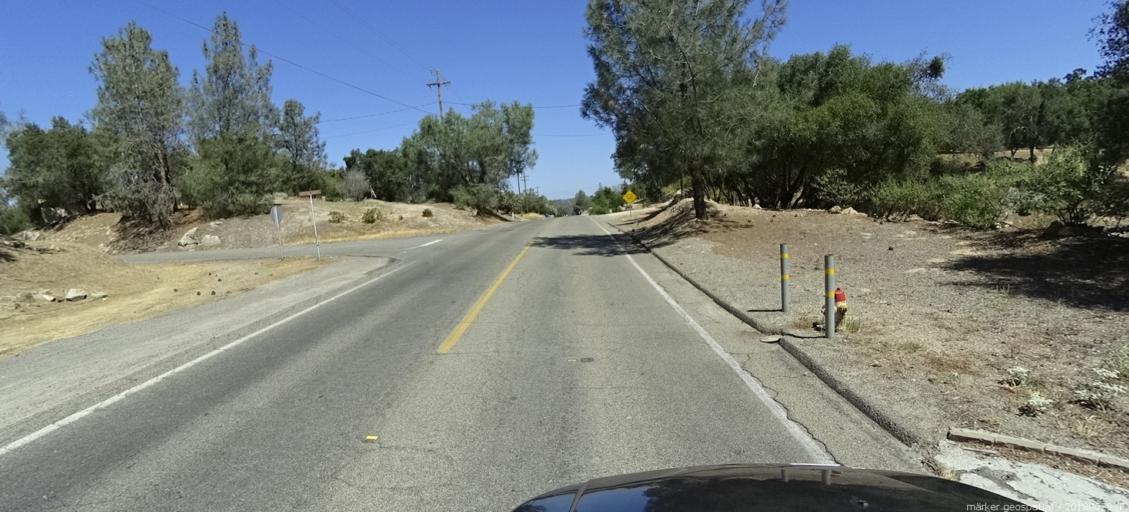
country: US
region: California
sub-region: Madera County
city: Yosemite Lakes
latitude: 37.1679
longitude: -119.7551
